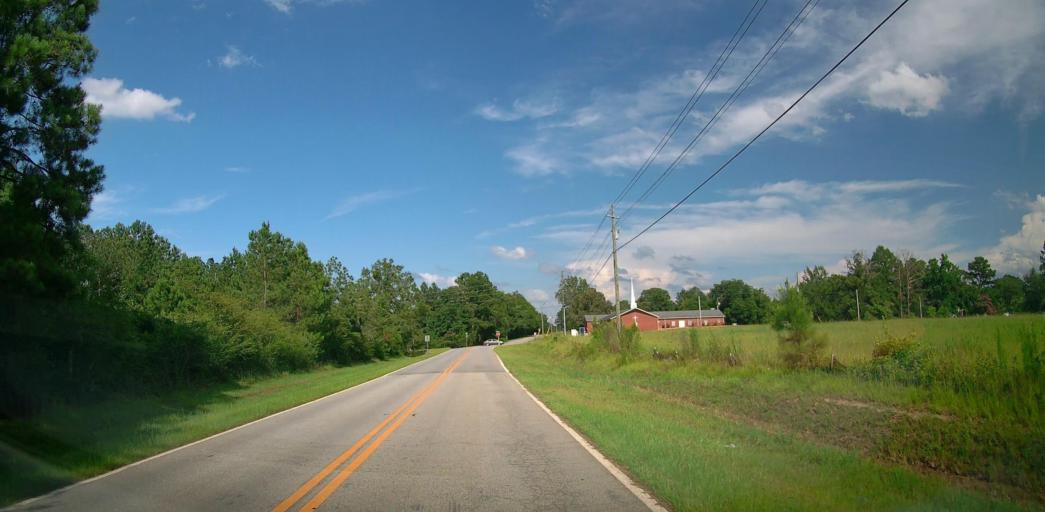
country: US
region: Georgia
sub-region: Houston County
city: Robins Air Force Base
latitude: 32.5242
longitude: -83.6161
